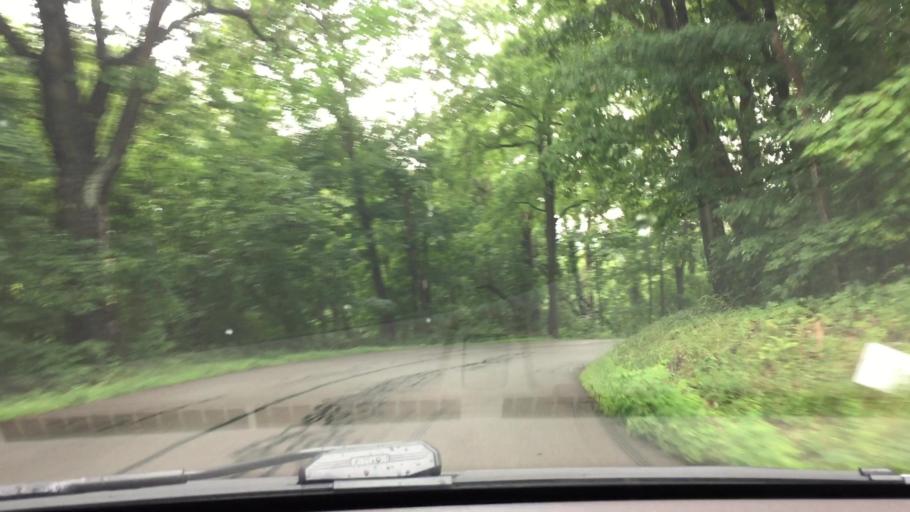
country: US
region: Pennsylvania
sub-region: Washington County
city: Muse
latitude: 40.3048
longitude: -80.1963
